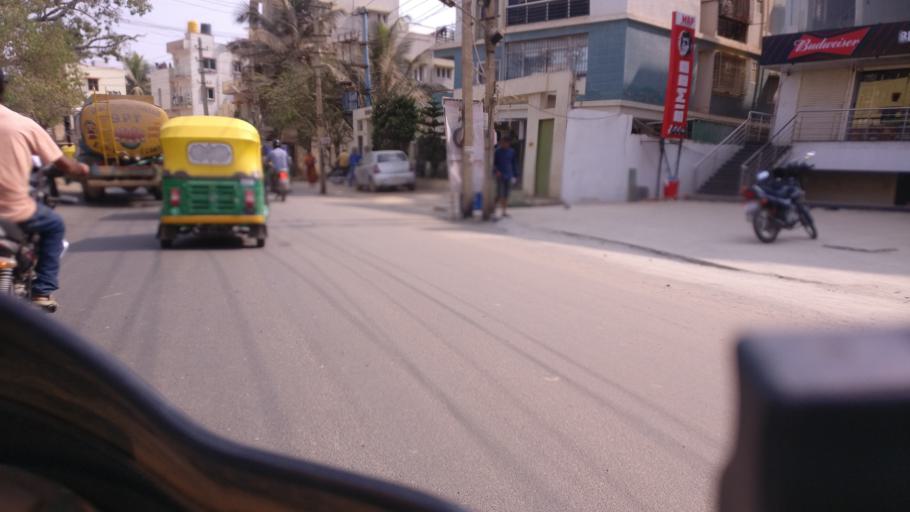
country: IN
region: Karnataka
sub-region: Bangalore Urban
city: Bangalore
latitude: 12.9085
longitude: 77.6762
